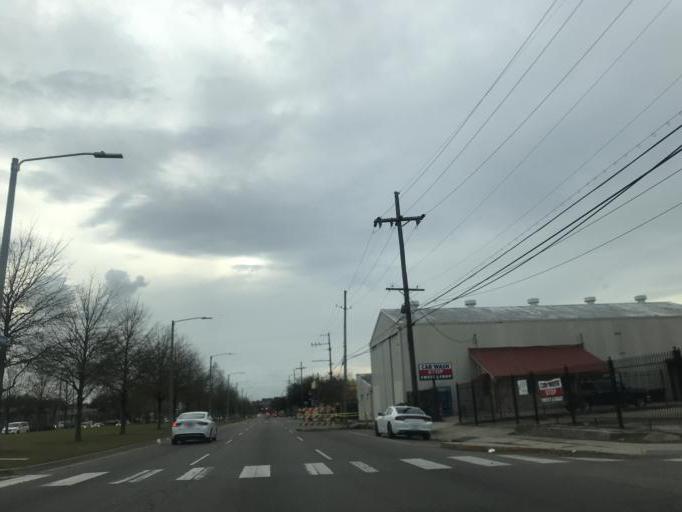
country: US
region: Louisiana
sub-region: Orleans Parish
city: New Orleans
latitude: 29.9441
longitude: -90.0921
